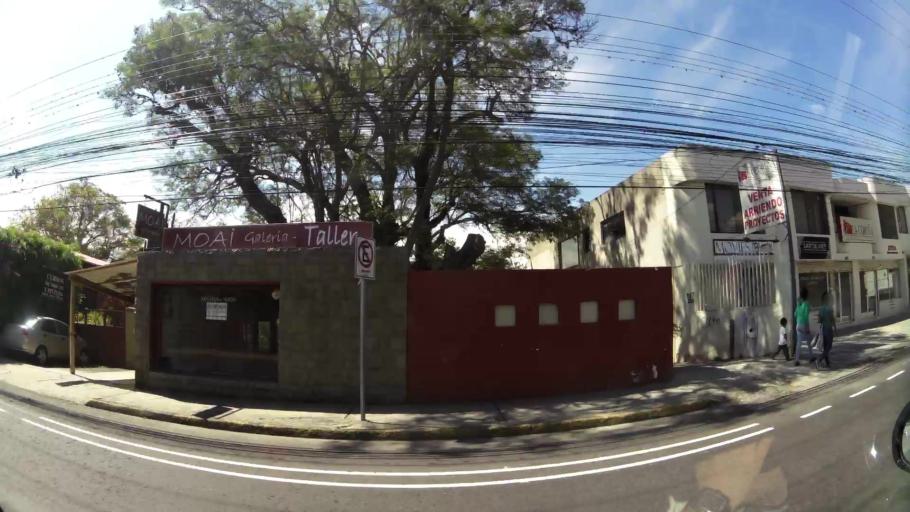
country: EC
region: Pichincha
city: Quito
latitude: -0.1989
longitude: -78.4317
